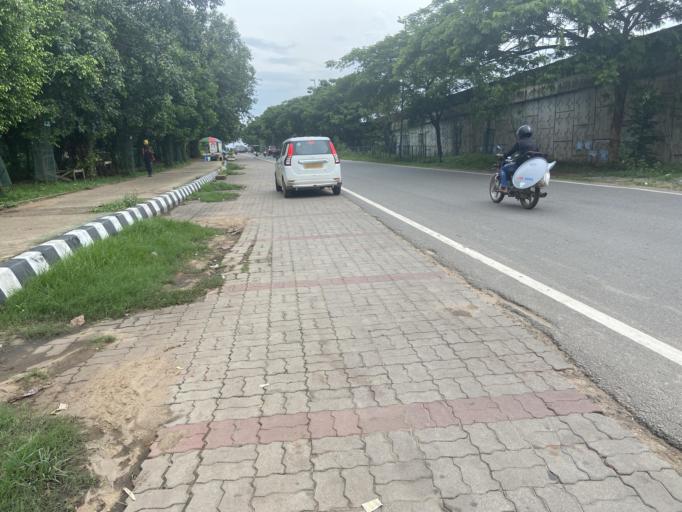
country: IN
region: Odisha
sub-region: Khordha
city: Bhubaneshwar
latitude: 20.2947
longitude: 85.8243
